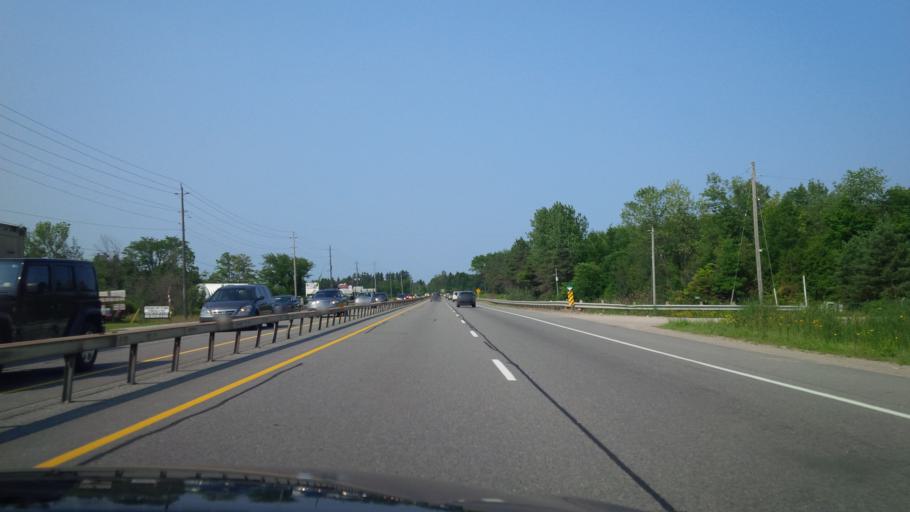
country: CA
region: Ontario
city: Barrie
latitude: 44.4766
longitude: -79.5383
